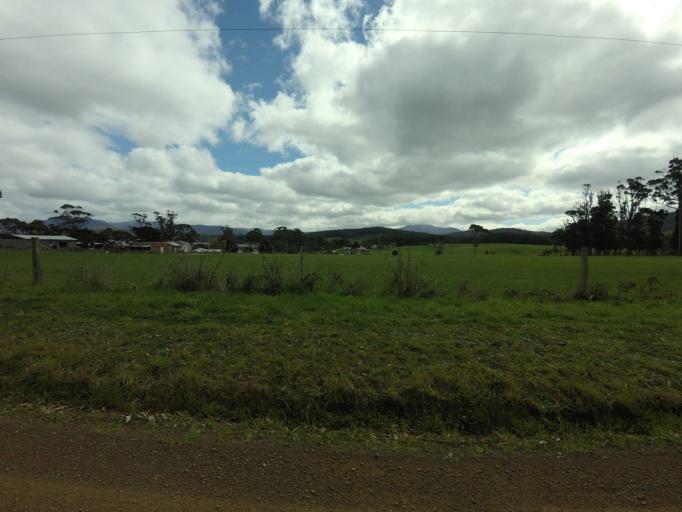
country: AU
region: Tasmania
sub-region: Huon Valley
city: Geeveston
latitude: -43.4360
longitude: 146.9860
